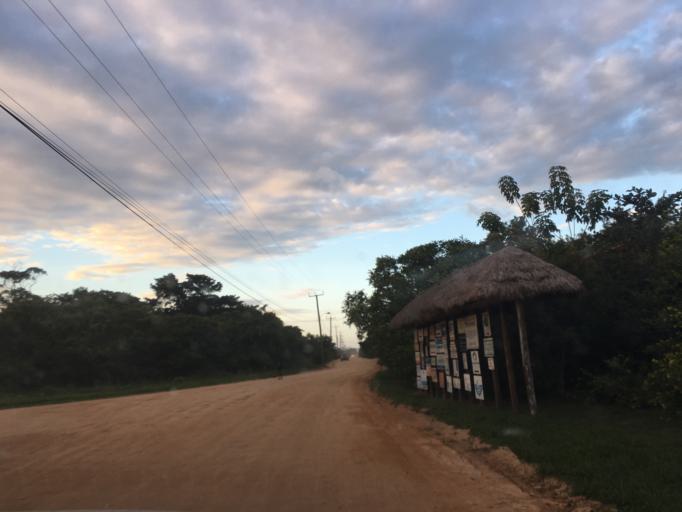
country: BZ
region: Stann Creek
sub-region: Dangriga
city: Dangriga
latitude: 16.8417
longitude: -88.2748
